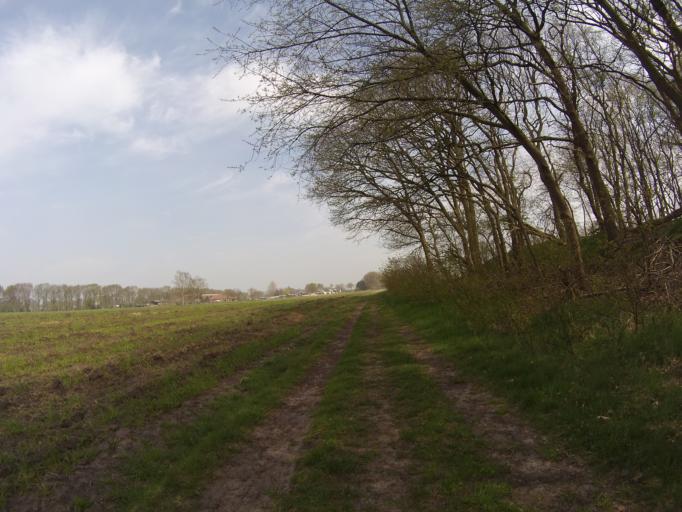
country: NL
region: Utrecht
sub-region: Gemeente Soest
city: Soest
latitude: 52.1563
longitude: 5.3315
